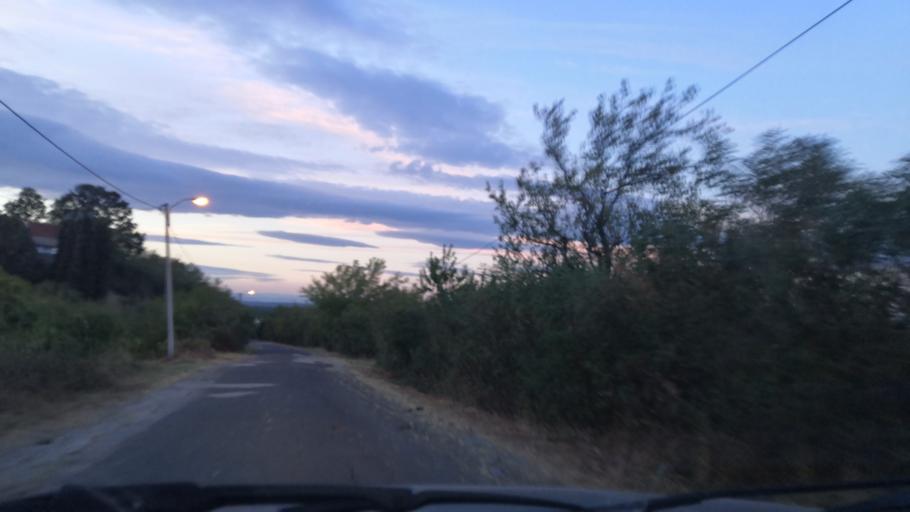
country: RO
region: Mehedinti
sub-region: Comuna Gogosu
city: Balta Verde
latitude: 44.3070
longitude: 22.5493
